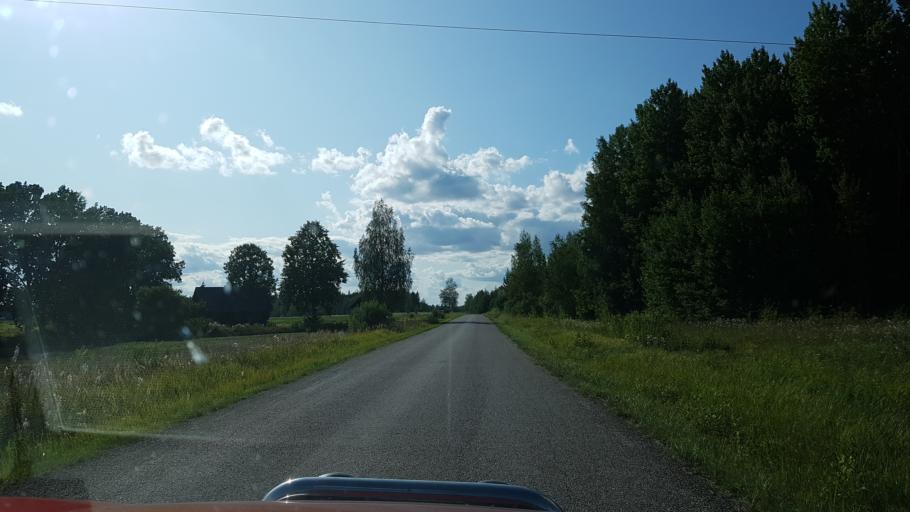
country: EE
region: Vorumaa
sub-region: Voru linn
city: Voru
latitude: 57.9184
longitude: 27.1598
